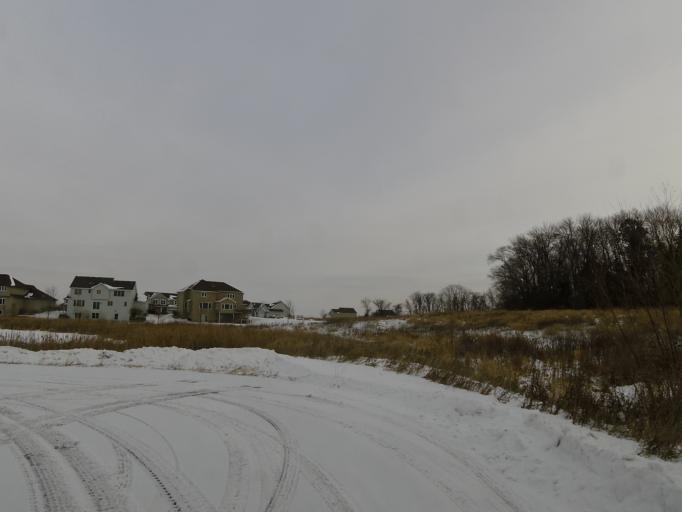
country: US
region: Minnesota
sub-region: Hennepin County
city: Saint Bonifacius
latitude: 44.8947
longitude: -93.7602
